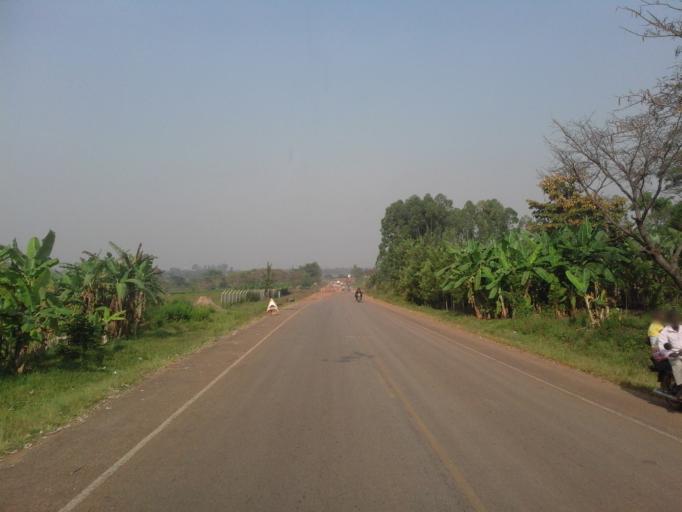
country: UG
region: Eastern Region
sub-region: Mbale District
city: Mbale
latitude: 1.0745
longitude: 34.1140
